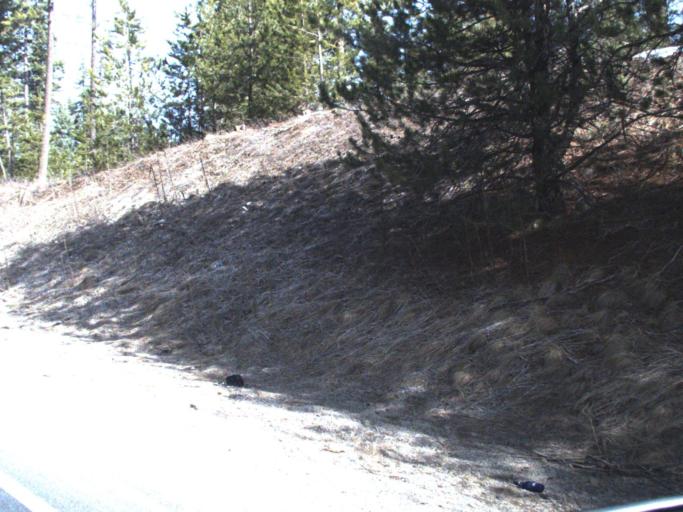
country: US
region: Washington
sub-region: Stevens County
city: Colville
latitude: 48.5135
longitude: -117.6821
